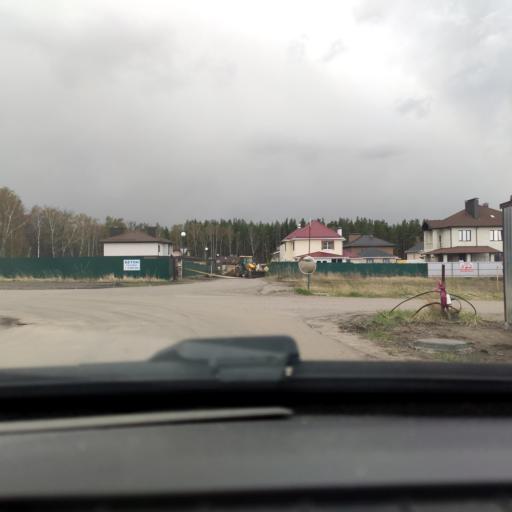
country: RU
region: Voronezj
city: Podgornoye
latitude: 51.7553
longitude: 39.1502
